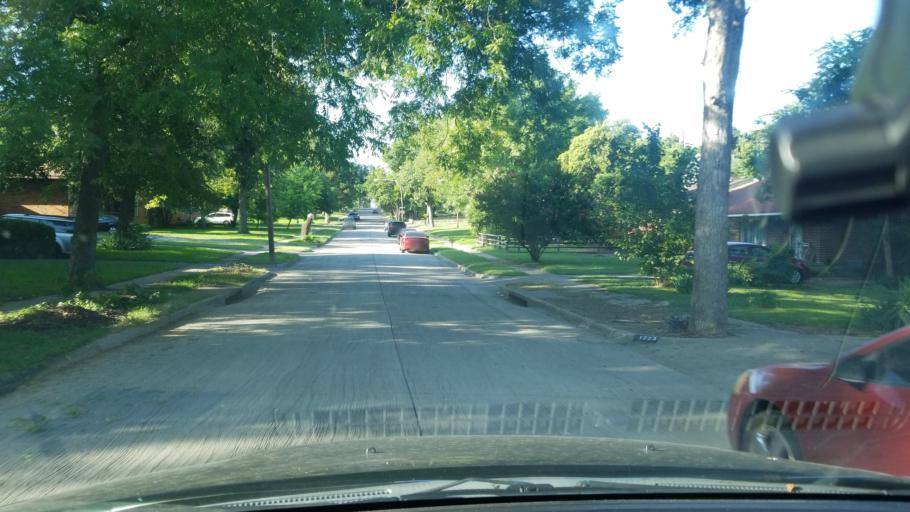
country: US
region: Texas
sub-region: Dallas County
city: Dallas
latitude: 32.7324
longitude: -96.8157
